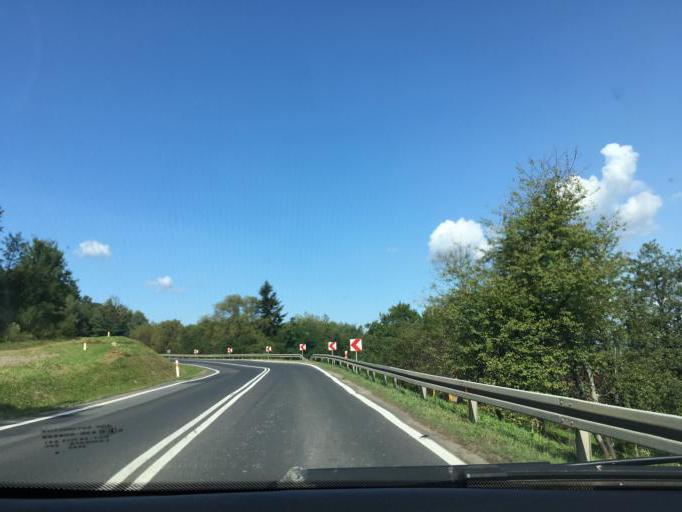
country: PL
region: Subcarpathian Voivodeship
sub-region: Powiat leski
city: Lesko
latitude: 49.4687
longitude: 22.3579
